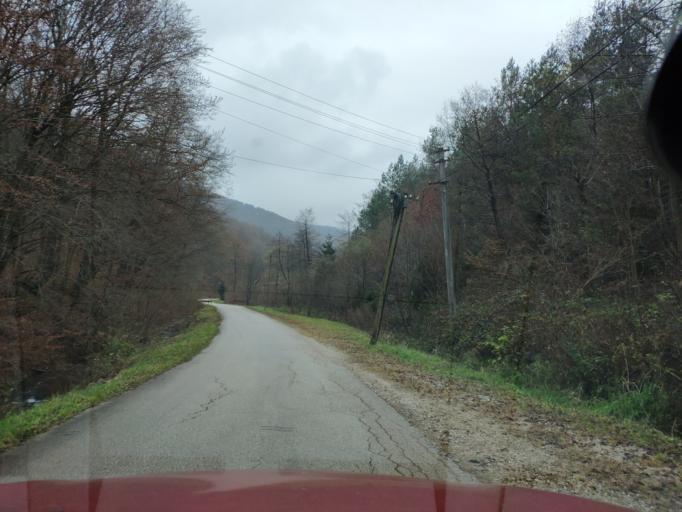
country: SK
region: Kosicky
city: Roznava
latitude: 48.7031
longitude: 20.5451
